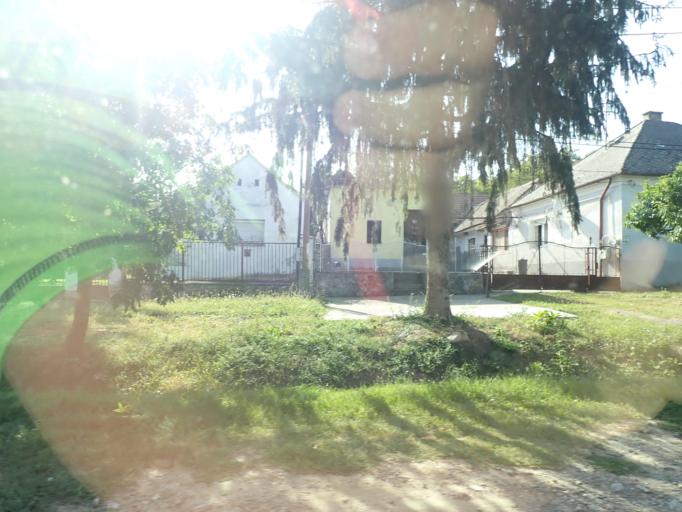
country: HU
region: Baranya
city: Boly
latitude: 45.9966
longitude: 18.5111
